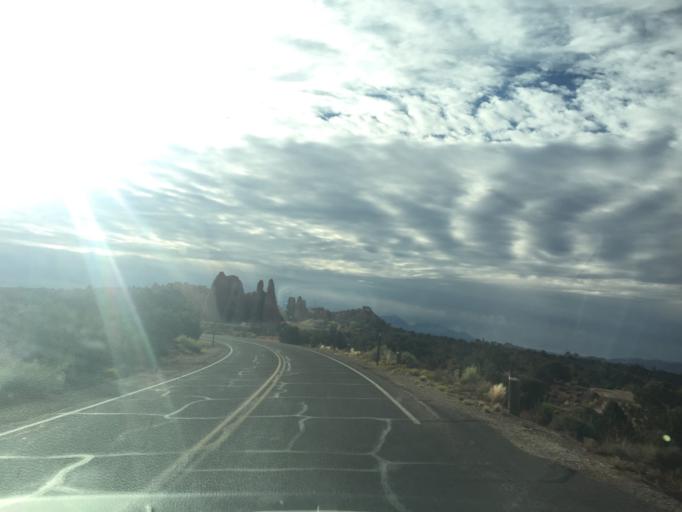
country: US
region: Utah
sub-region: Grand County
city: Moab
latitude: 38.7684
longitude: -109.5886
